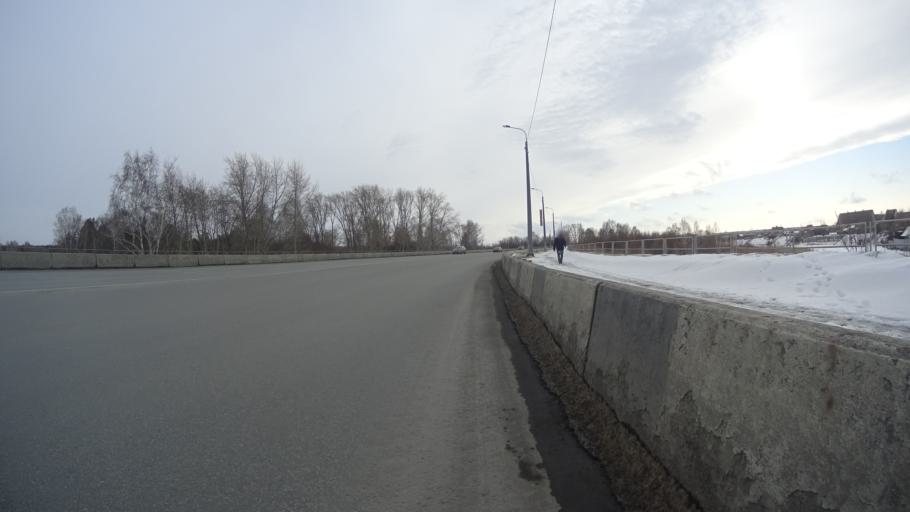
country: RU
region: Chelyabinsk
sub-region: Gorod Chelyabinsk
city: Chelyabinsk
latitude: 55.1524
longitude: 61.3196
